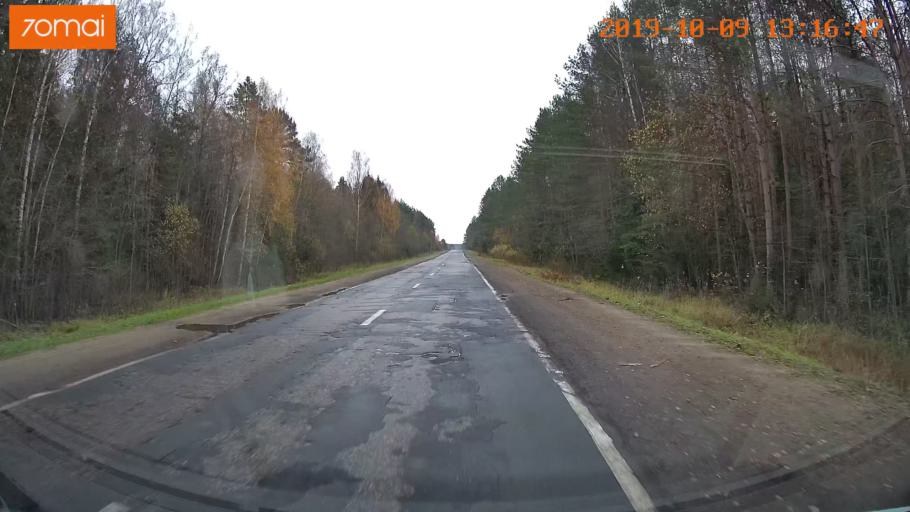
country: RU
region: Jaroslavl
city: Lyubim
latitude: 58.3586
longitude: 40.7706
